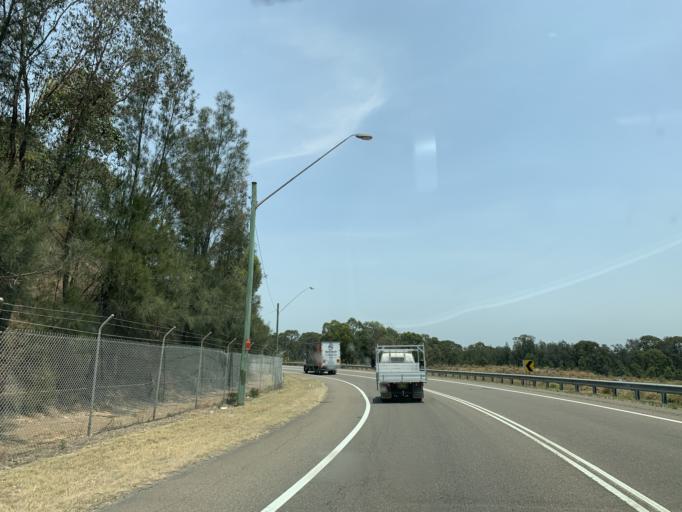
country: AU
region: New South Wales
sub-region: Blacktown
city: Doonside
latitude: -33.8020
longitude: 150.8657
